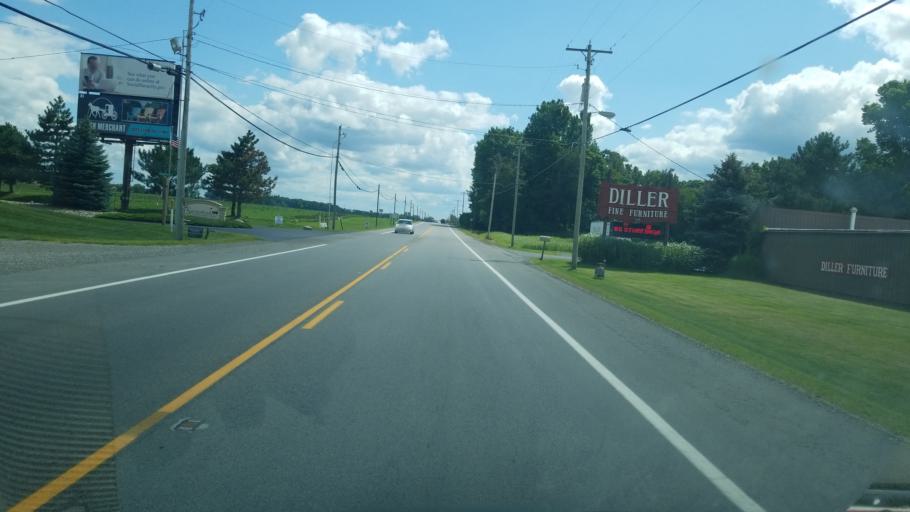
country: US
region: Ohio
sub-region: Allen County
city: Lima
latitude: 40.7961
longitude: -84.1089
